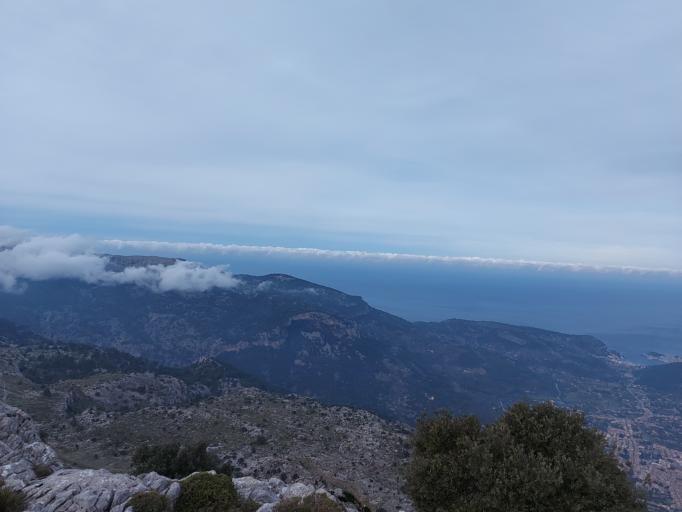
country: ES
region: Balearic Islands
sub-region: Illes Balears
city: Soller
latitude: 39.7433
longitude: 2.7325
